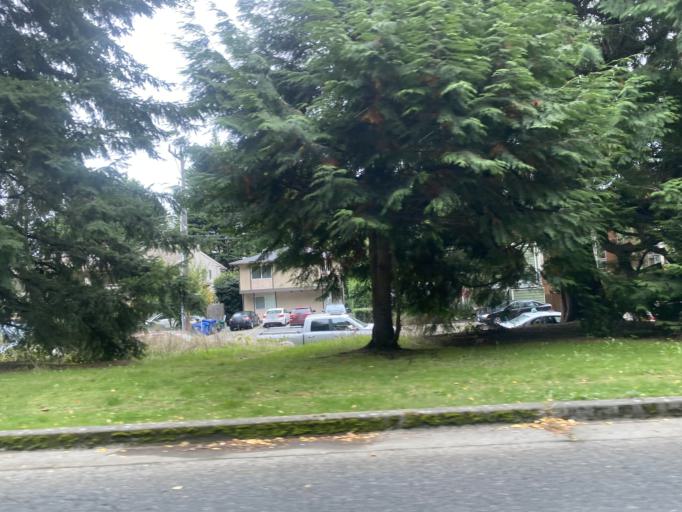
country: US
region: Washington
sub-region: King County
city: Seattle
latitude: 47.6591
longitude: -122.4039
